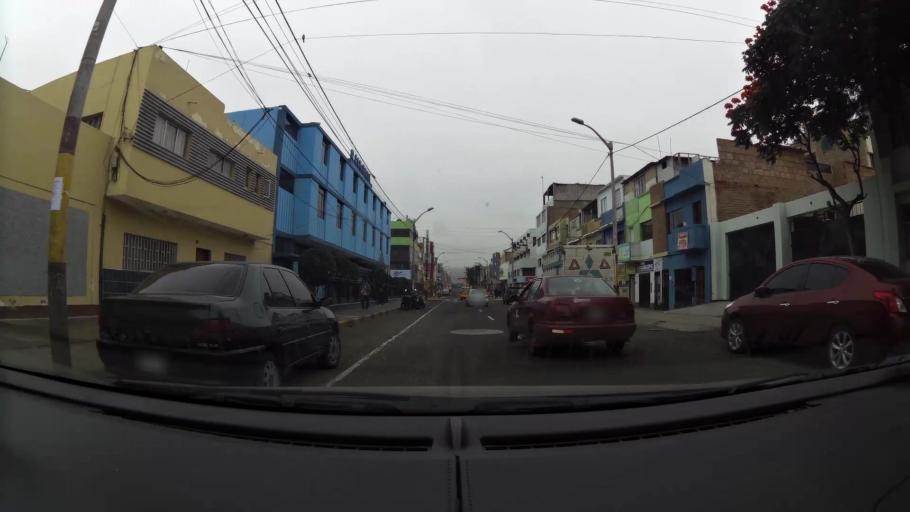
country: PE
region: Ancash
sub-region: Provincia de Santa
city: Chimbote
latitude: -9.0735
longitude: -78.5938
